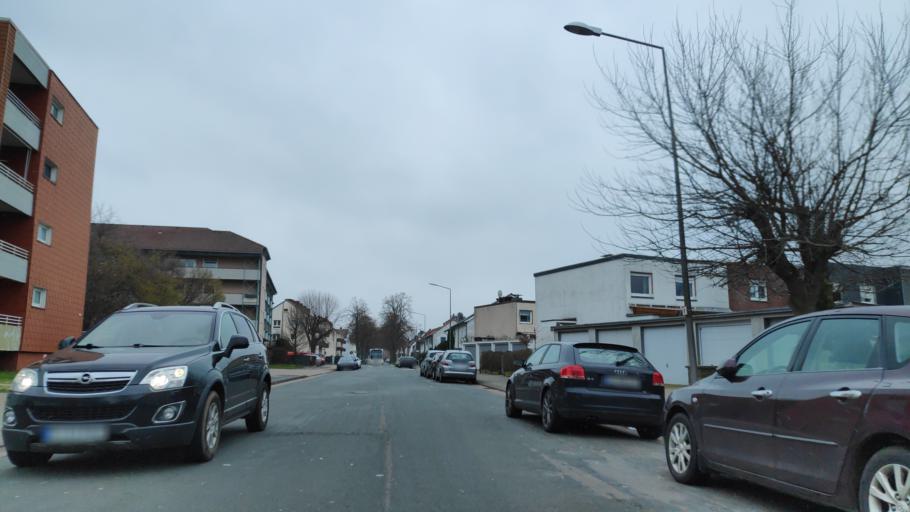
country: DE
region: North Rhine-Westphalia
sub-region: Regierungsbezirk Detmold
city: Minden
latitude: 52.2929
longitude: 8.8895
